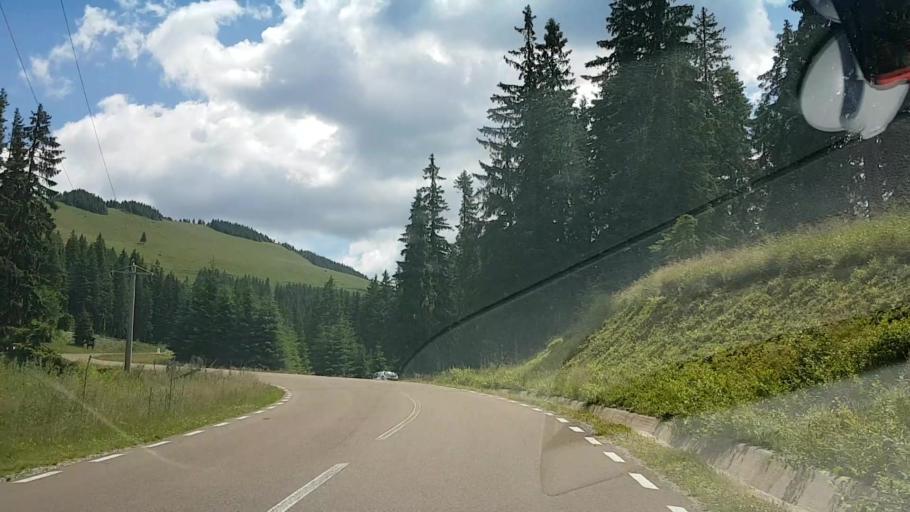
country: RO
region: Suceava
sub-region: Comuna Sadova
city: Sadova
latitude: 47.4580
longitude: 25.5207
